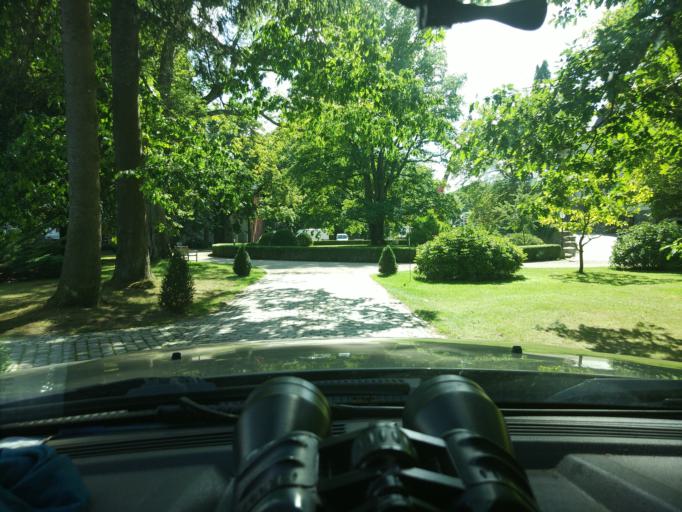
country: PL
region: Pomeranian Voivodeship
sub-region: Powiat wejherowski
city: Choczewo
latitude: 54.7459
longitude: 17.7974
